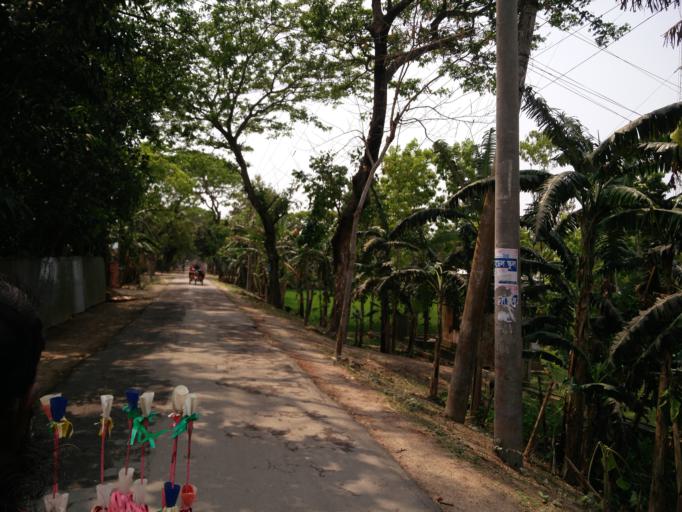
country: BD
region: Dhaka
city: Sherpur
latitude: 24.9583
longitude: 90.1719
